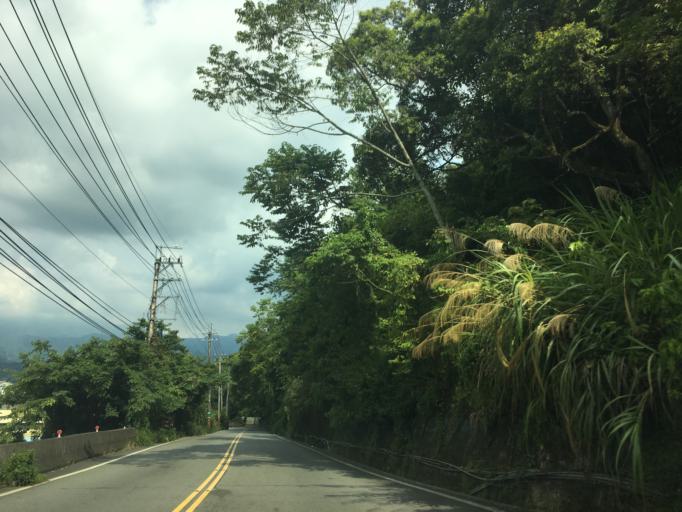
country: TW
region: Taiwan
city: Fengyuan
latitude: 24.2547
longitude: 120.8109
